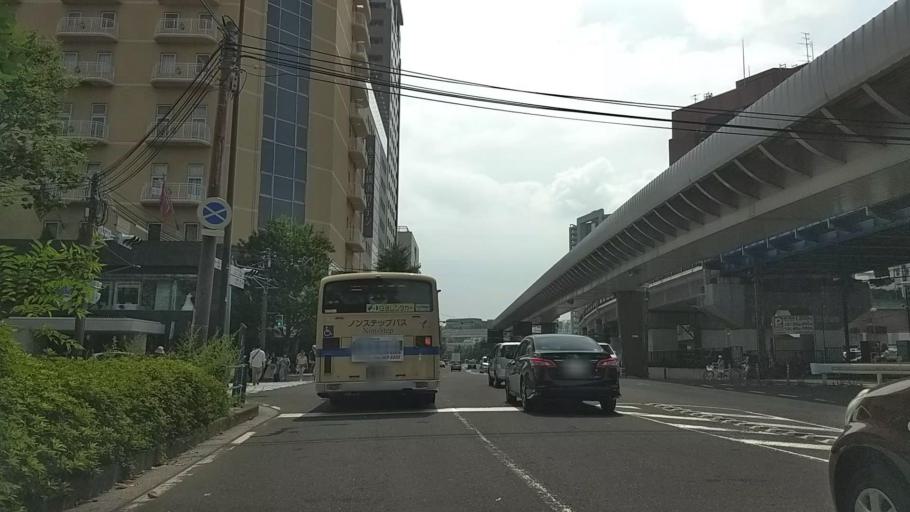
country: JP
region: Kanagawa
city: Yokohama
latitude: 35.4421
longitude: 139.6403
